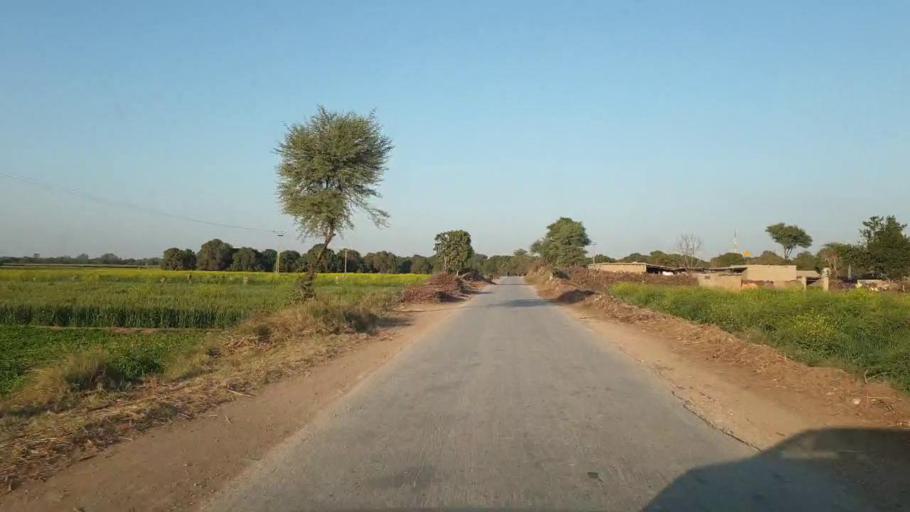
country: PK
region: Sindh
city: Tando Allahyar
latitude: 25.3895
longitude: 68.7585
